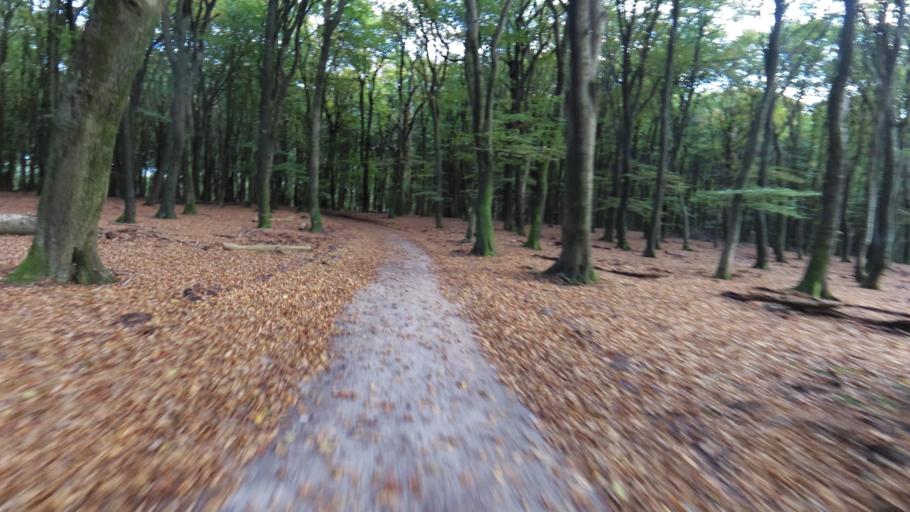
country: NL
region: Gelderland
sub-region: Gemeente Nunspeet
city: Nunspeet
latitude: 52.3189
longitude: 5.8329
